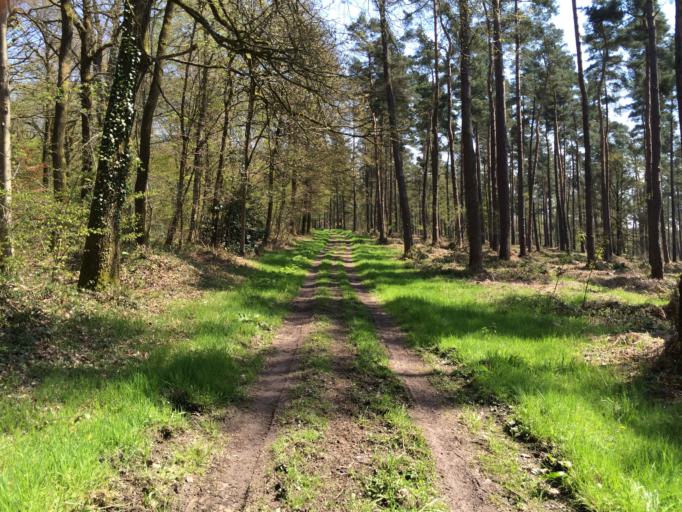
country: BE
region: Wallonia
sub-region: Province de Namur
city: Yvoir
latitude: 50.3370
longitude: 4.9526
